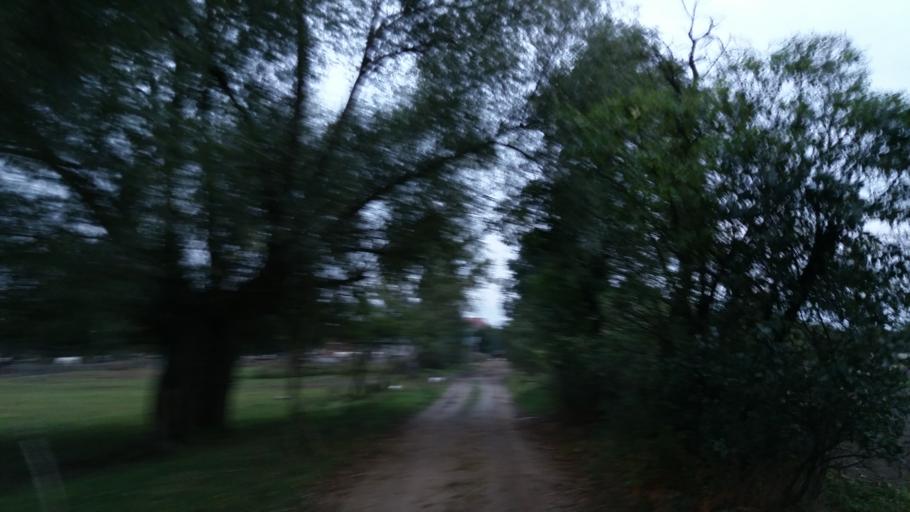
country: PL
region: West Pomeranian Voivodeship
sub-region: Powiat choszczenski
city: Choszczno
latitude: 53.0908
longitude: 15.4011
